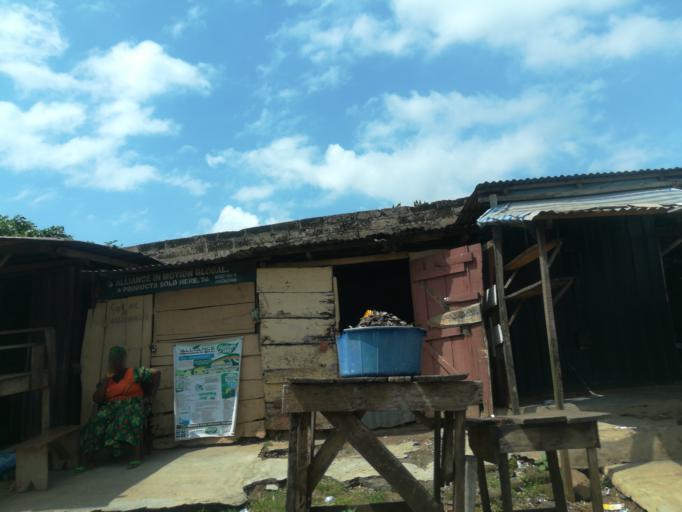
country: NG
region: Oyo
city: Egbeda
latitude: 7.4246
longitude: 3.9951
